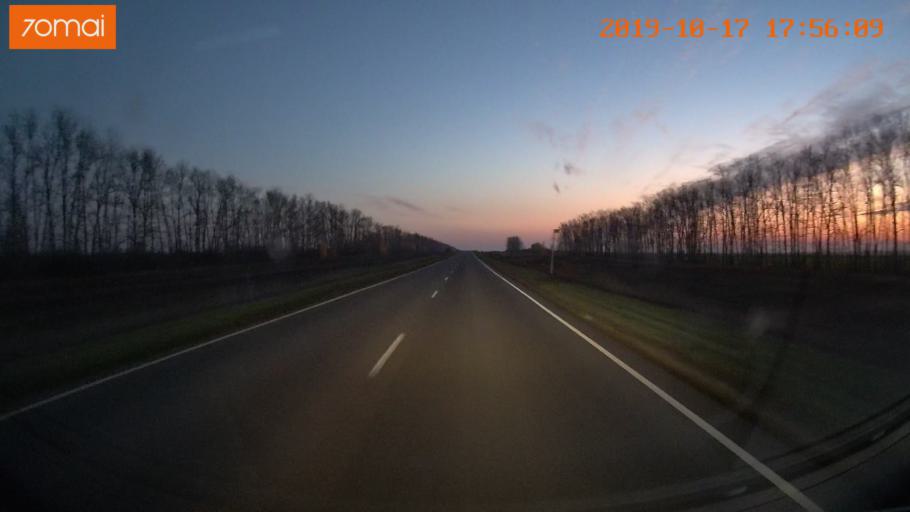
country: RU
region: Tula
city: Kurkino
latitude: 53.5836
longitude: 38.6501
